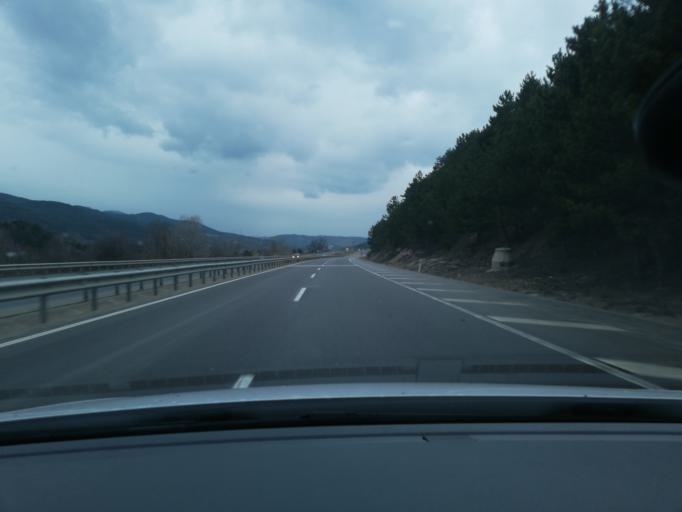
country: TR
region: Bolu
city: Yenicaga
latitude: 40.7463
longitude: 31.8739
